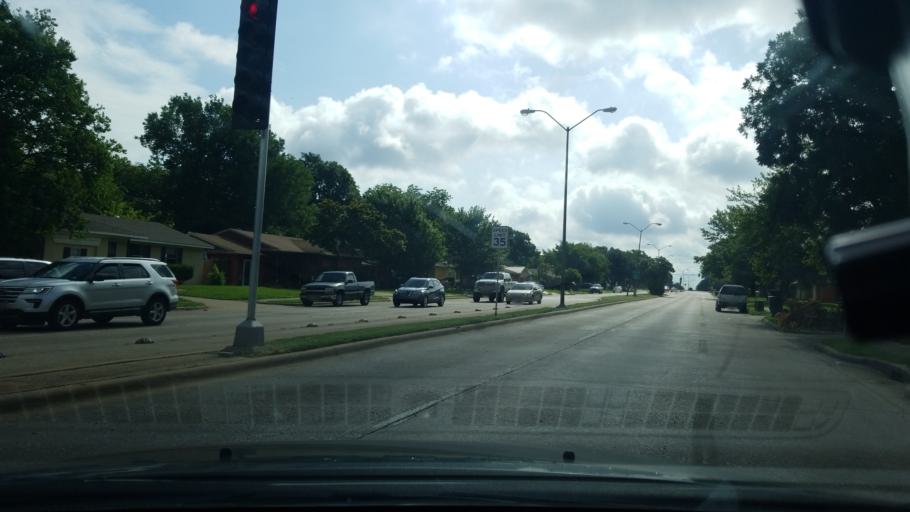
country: US
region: Texas
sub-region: Dallas County
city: Mesquite
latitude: 32.8214
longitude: -96.6680
